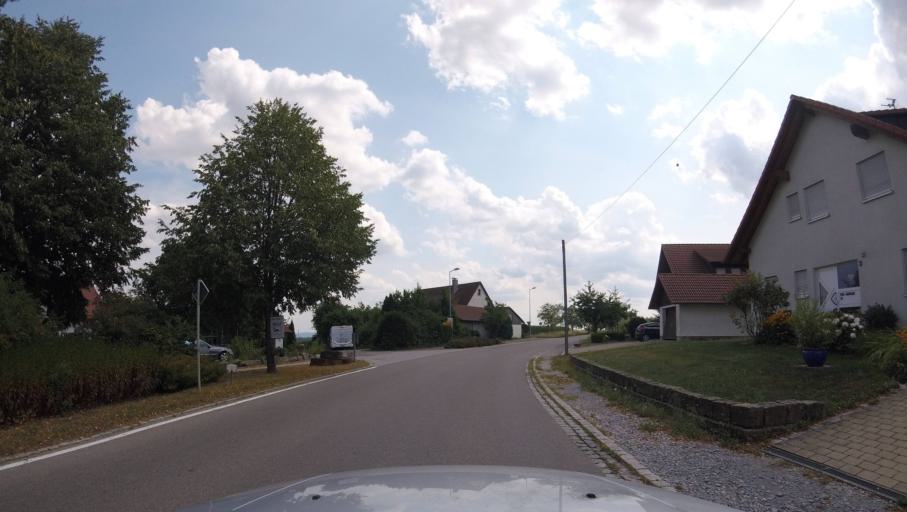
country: DE
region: Baden-Wuerttemberg
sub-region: Regierungsbezirk Stuttgart
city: Spraitbach
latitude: 48.8953
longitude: 9.7242
